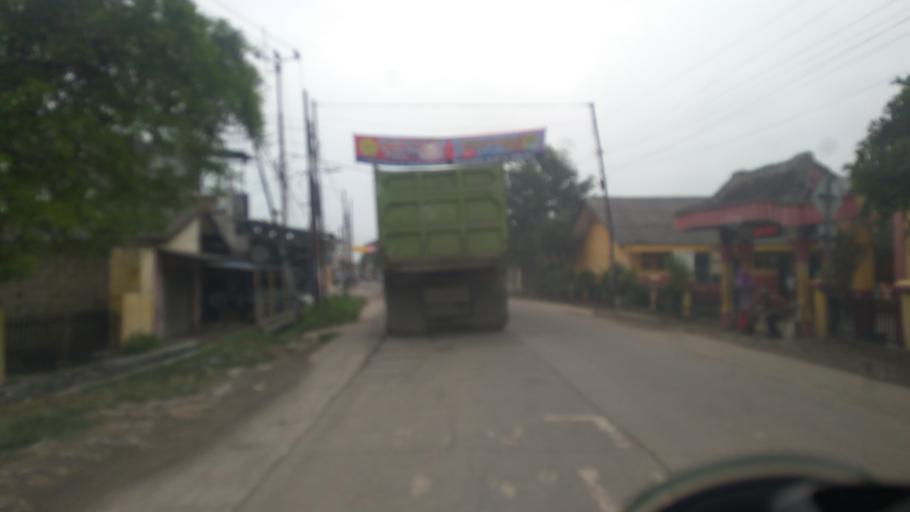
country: ID
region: West Java
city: Bekasi
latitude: -6.1982
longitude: 107.0380
